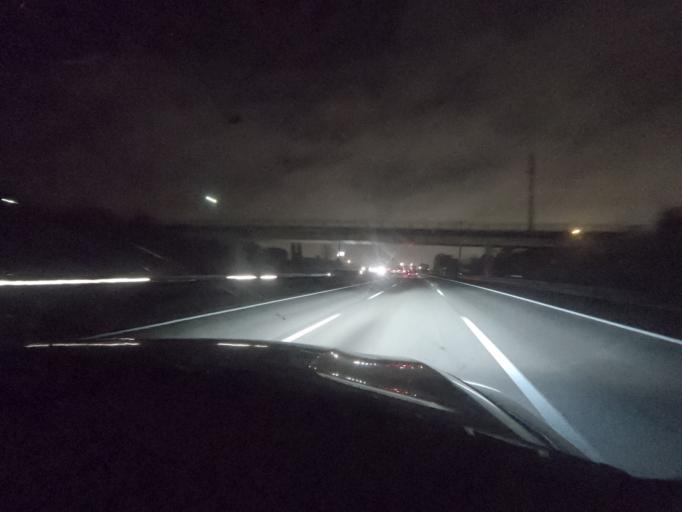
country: PT
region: Lisbon
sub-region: Alenquer
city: Carregado
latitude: 39.0377
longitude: -8.9569
